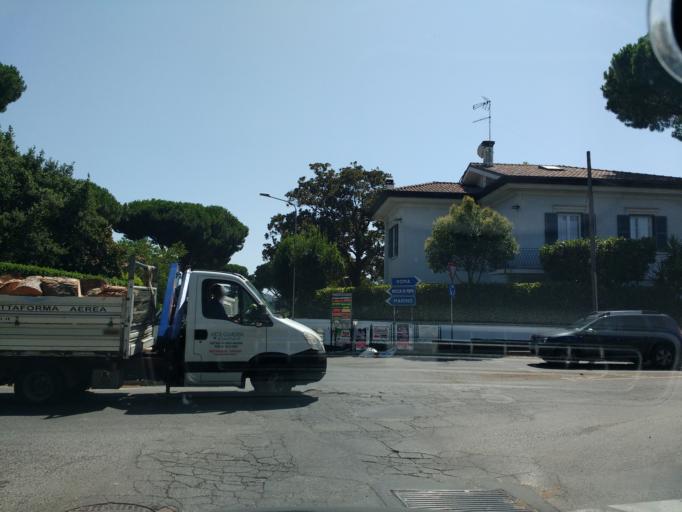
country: IT
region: Latium
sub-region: Citta metropolitana di Roma Capitale
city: Grottaferrata
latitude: 41.7919
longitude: 12.6828
